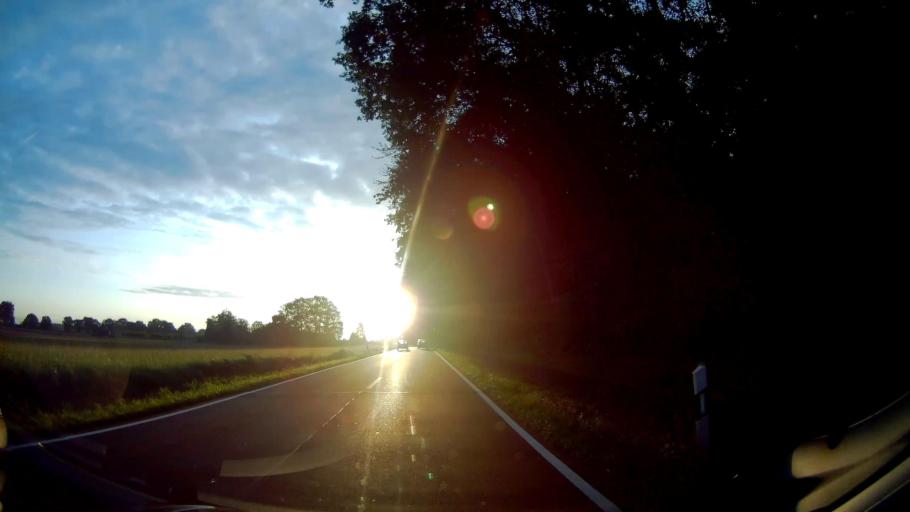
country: DE
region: North Rhine-Westphalia
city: Marl
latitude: 51.6240
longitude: 7.0892
